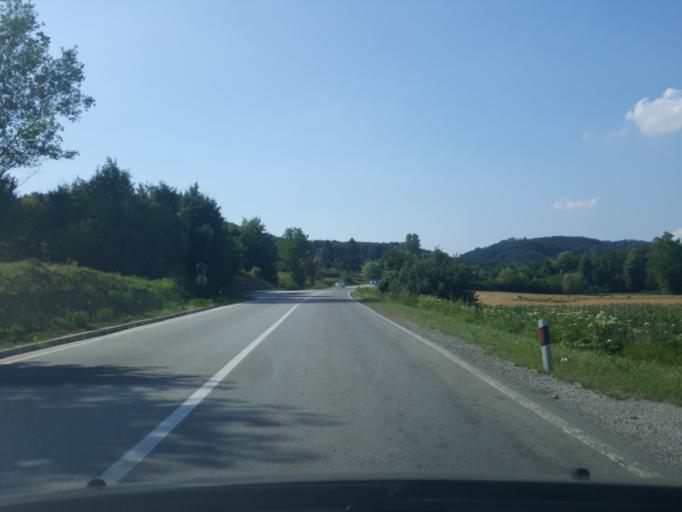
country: RS
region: Central Serbia
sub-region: Moravicki Okrug
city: Gornji Milanovac
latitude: 44.0834
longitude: 20.4811
